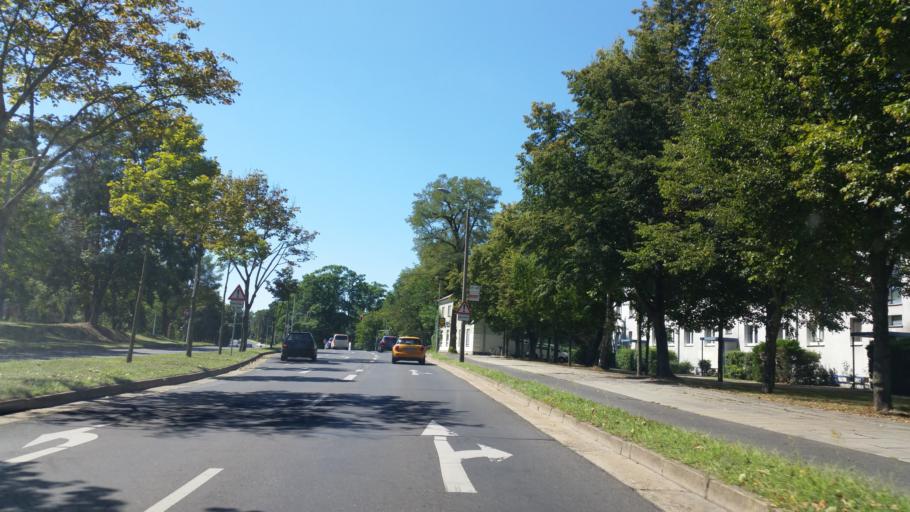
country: DE
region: Brandenburg
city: Cottbus
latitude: 51.7291
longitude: 14.3233
